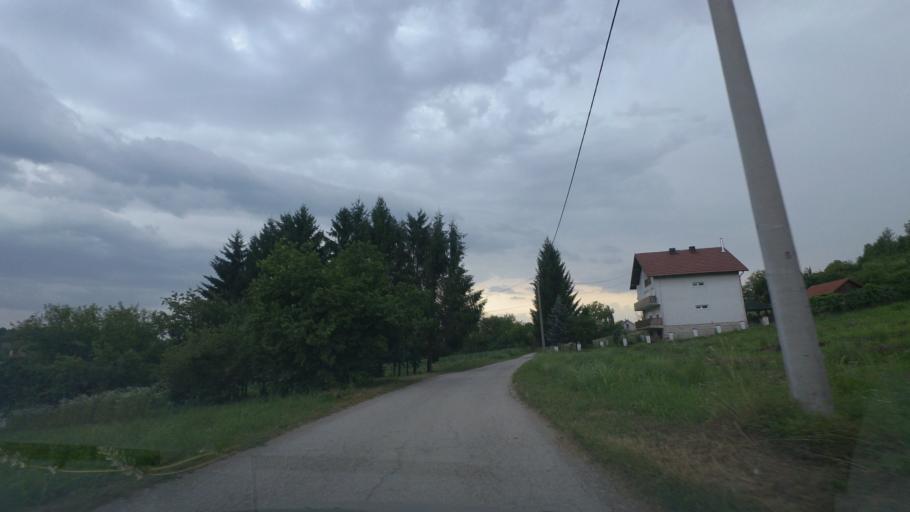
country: HR
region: Karlovacka
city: Vojnic
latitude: 45.3844
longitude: 15.6070
